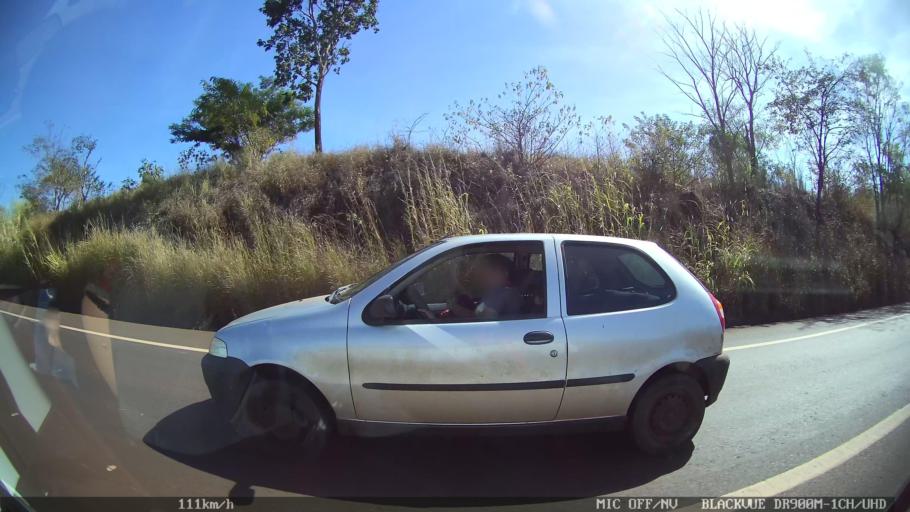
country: BR
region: Sao Paulo
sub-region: Sao Joaquim Da Barra
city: Sao Joaquim da Barra
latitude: -20.5551
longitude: -47.6809
